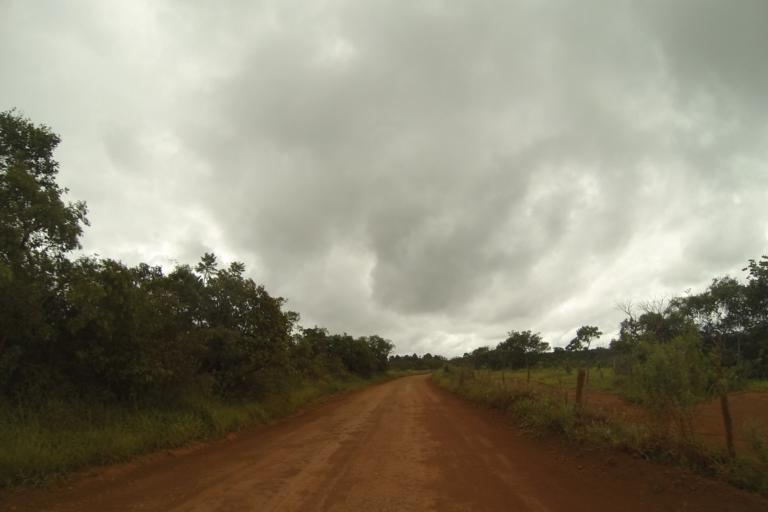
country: BR
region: Minas Gerais
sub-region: Campos Altos
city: Campos Altos
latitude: -19.8057
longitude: -46.3509
